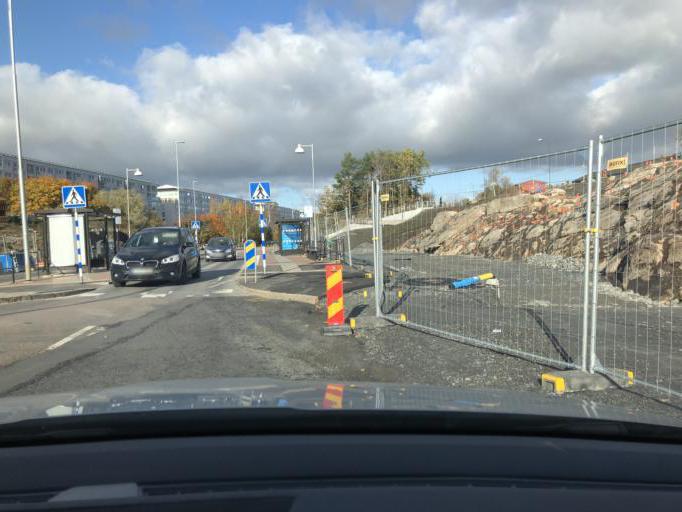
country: SE
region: Vaestra Goetaland
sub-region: Goteborg
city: Gardsten
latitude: 57.8034
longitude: 12.0337
